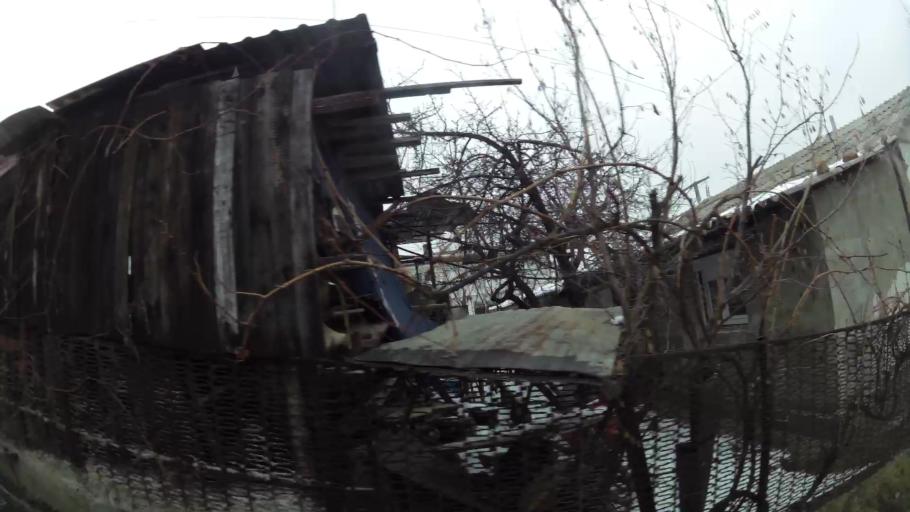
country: MK
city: Kondovo
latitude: 42.0395
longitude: 21.3464
